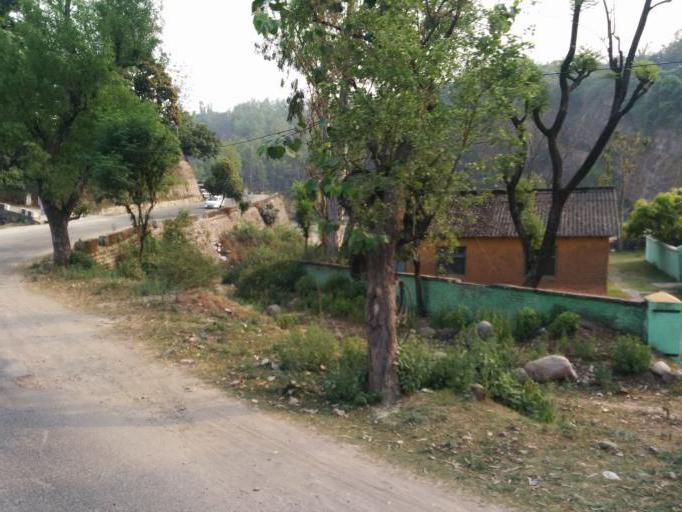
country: IN
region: Himachal Pradesh
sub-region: Kangra
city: Kotla
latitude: 32.2368
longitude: 76.0480
